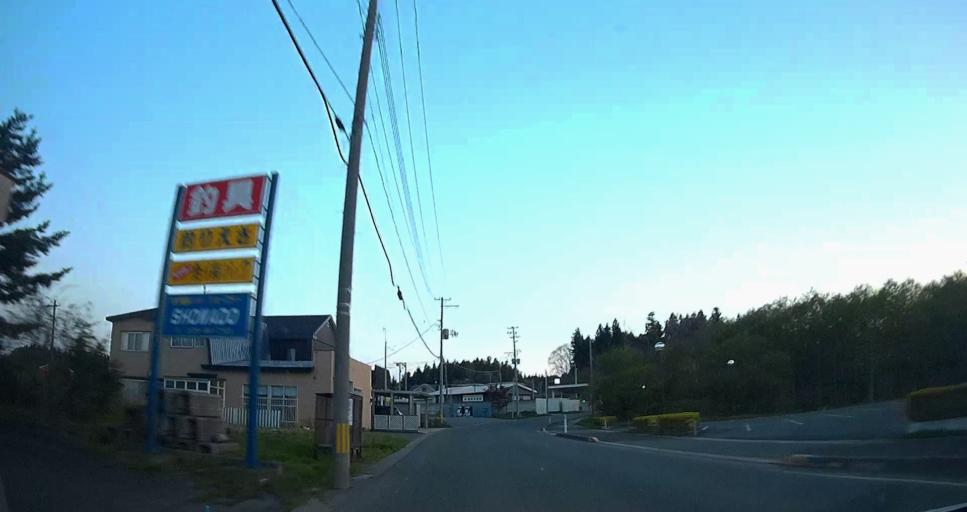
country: JP
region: Aomori
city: Misawa
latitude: 40.8675
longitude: 141.1107
